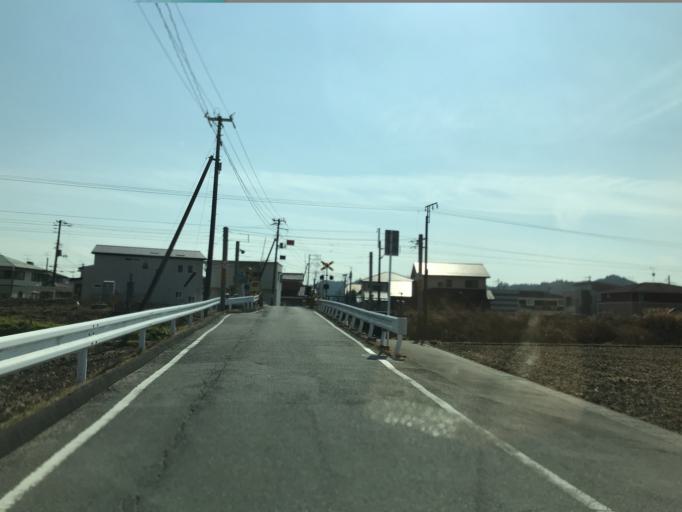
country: JP
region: Fukushima
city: Iwaki
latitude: 37.0660
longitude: 140.9318
